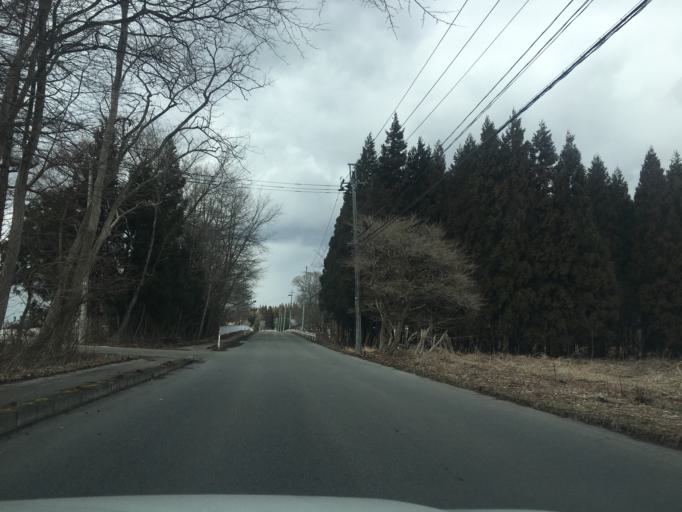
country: JP
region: Akita
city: Takanosu
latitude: 40.1820
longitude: 140.3432
